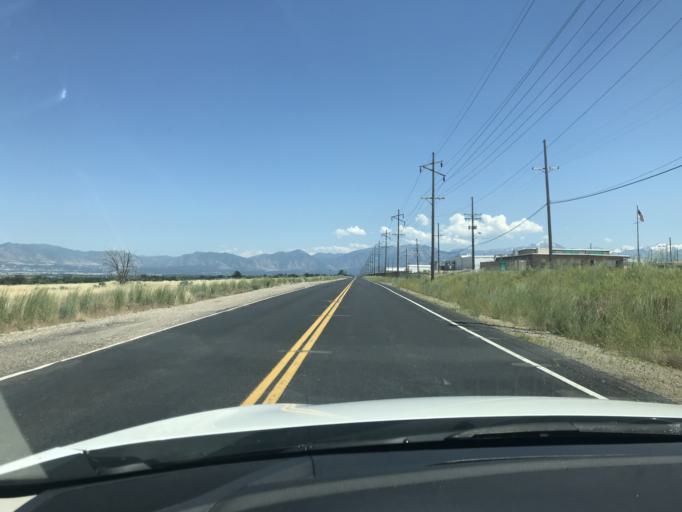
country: US
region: Utah
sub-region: Salt Lake County
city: Magna
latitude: 40.6820
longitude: -112.0734
